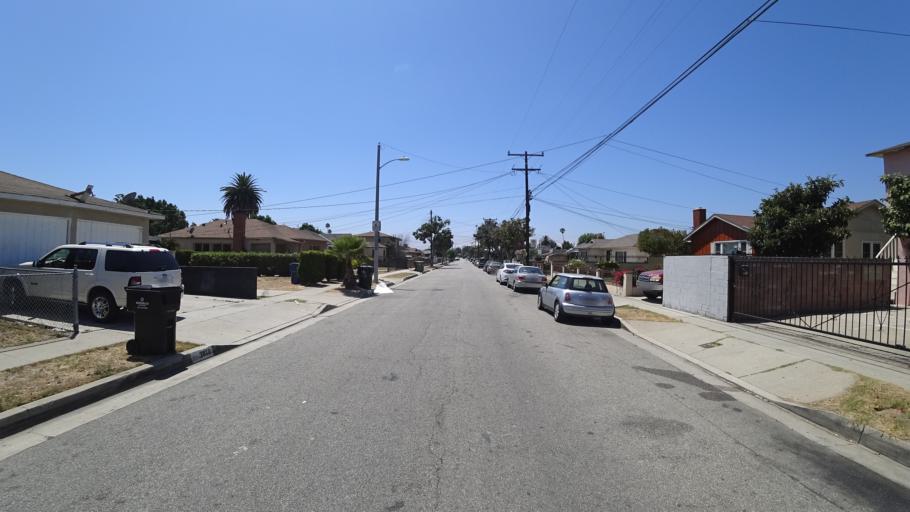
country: US
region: California
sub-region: Los Angeles County
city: Lennox
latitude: 33.9368
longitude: -118.3396
